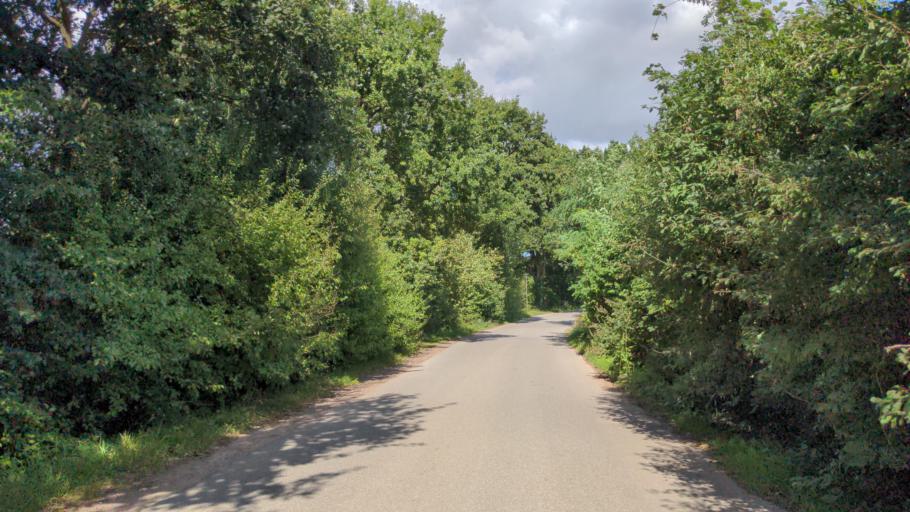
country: DE
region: Schleswig-Holstein
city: Beschendorf
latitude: 54.1972
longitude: 10.8225
